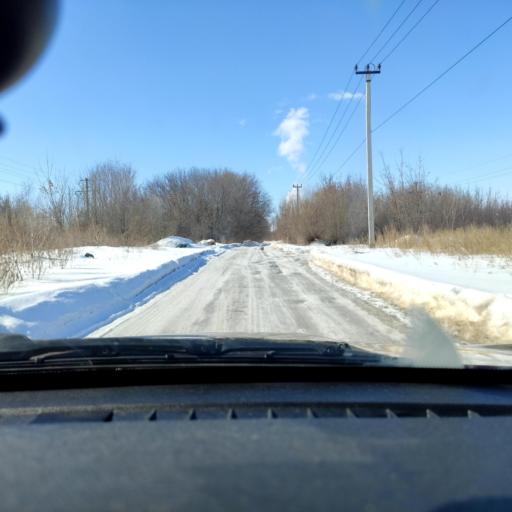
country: RU
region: Samara
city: Tol'yatti
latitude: 53.5659
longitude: 49.3175
